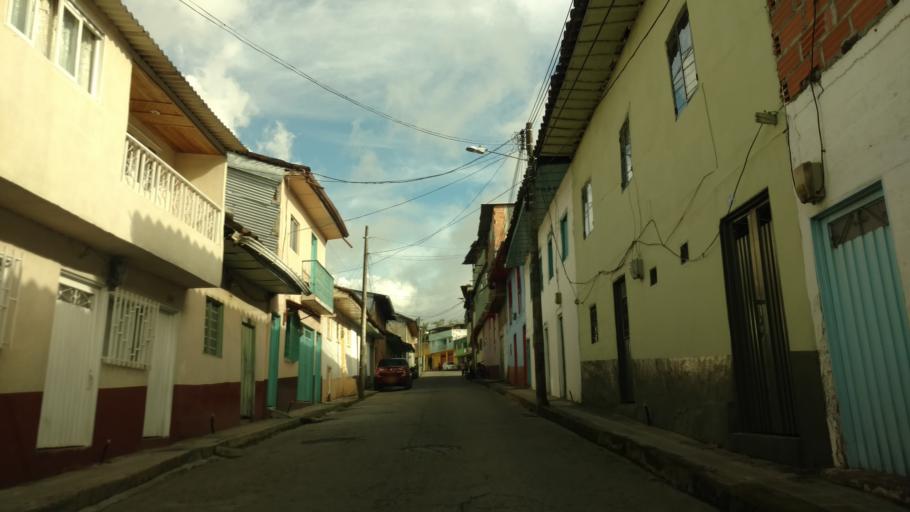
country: CO
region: Caldas
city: Aguadas
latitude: 5.6083
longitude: -75.4544
